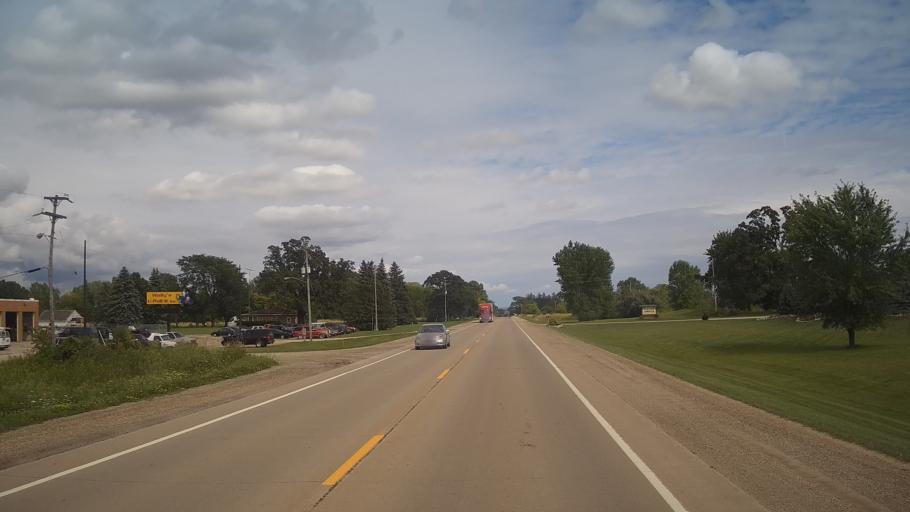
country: US
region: Wisconsin
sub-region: Winnebago County
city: Oshkosh
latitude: 44.0331
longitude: -88.6398
